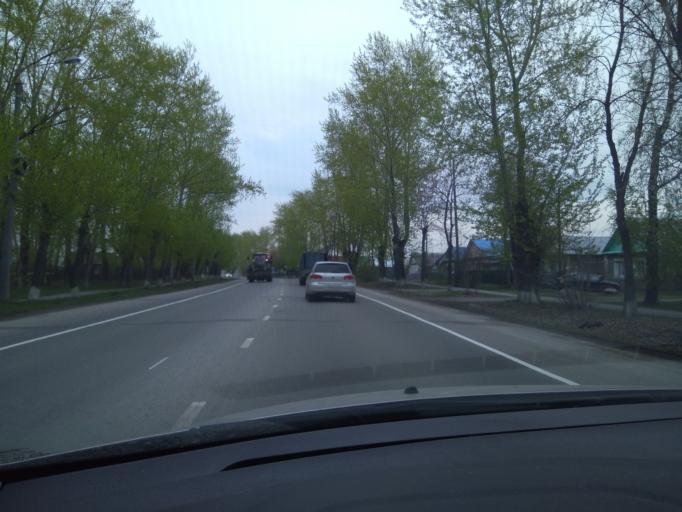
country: RU
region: Sverdlovsk
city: Bogdanovich
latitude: 56.7659
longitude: 62.0602
